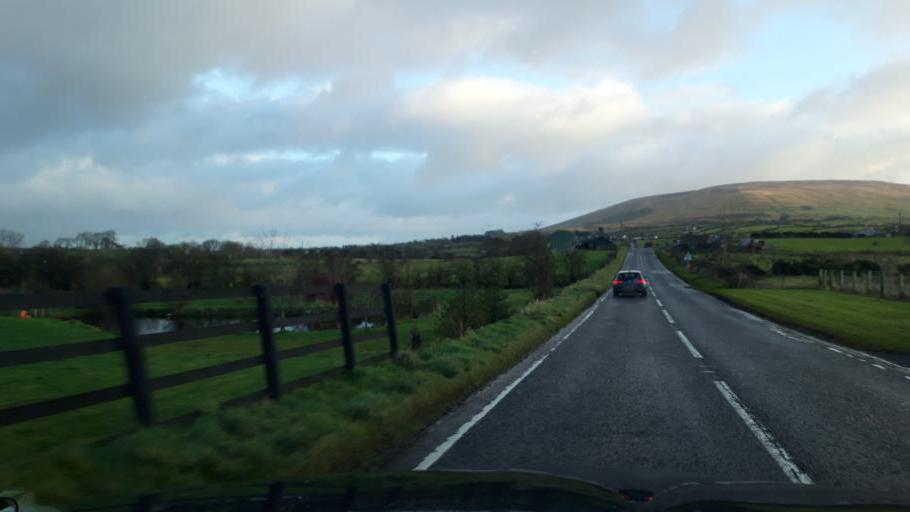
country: GB
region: Northern Ireland
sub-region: Moyle District
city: Ballycastle
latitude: 55.1448
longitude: -6.3163
